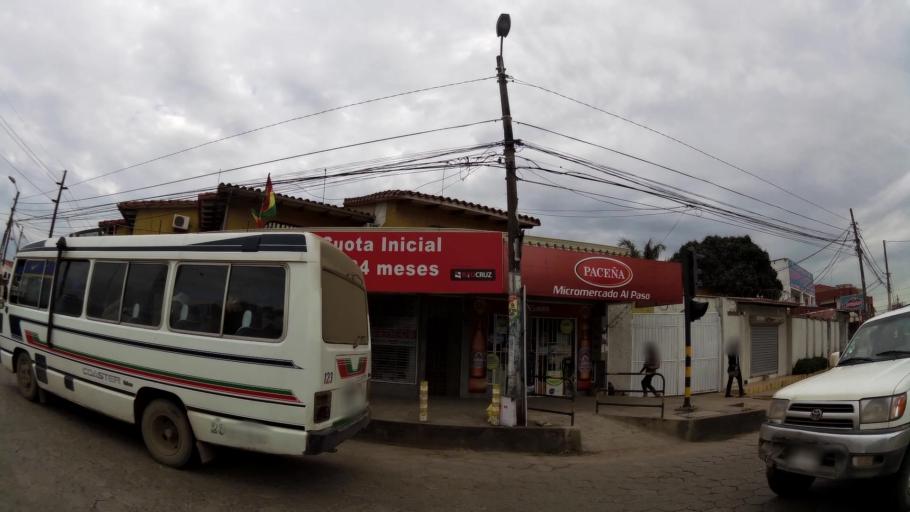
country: BO
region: Santa Cruz
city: Santa Cruz de la Sierra
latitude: -17.7606
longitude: -63.1675
